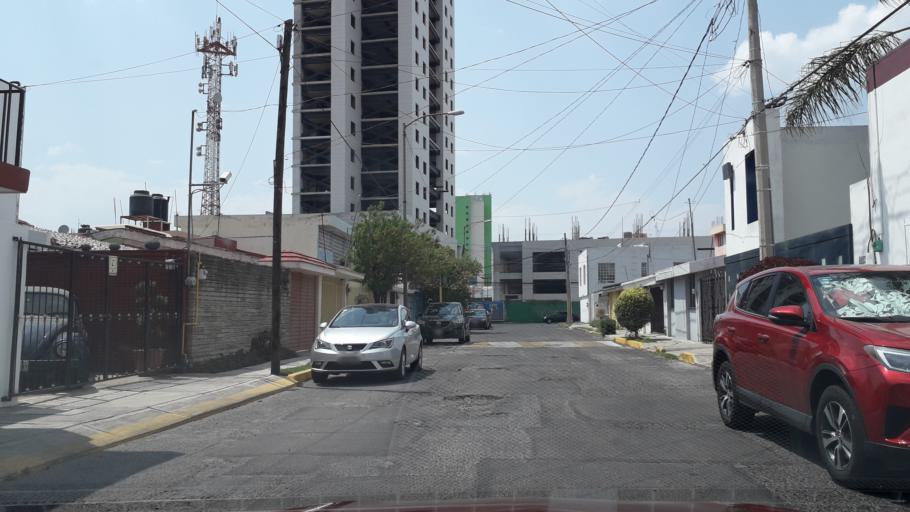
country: MX
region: Puebla
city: Puebla
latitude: 19.0336
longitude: -98.2212
